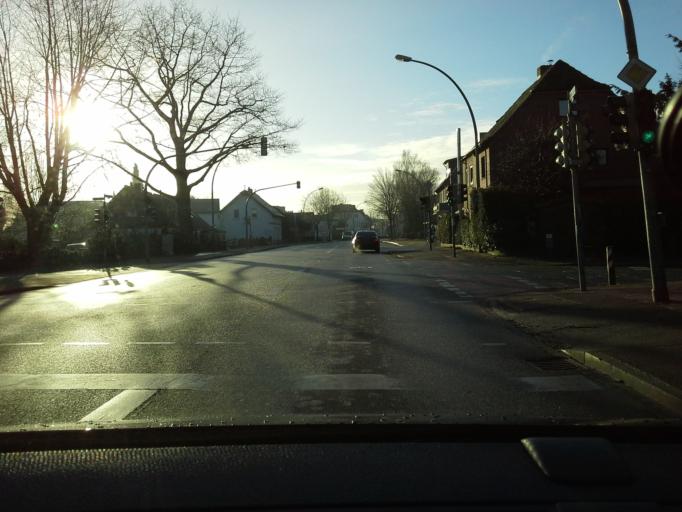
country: DE
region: Schleswig-Holstein
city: Pinneberg
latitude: 53.6719
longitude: 9.7941
